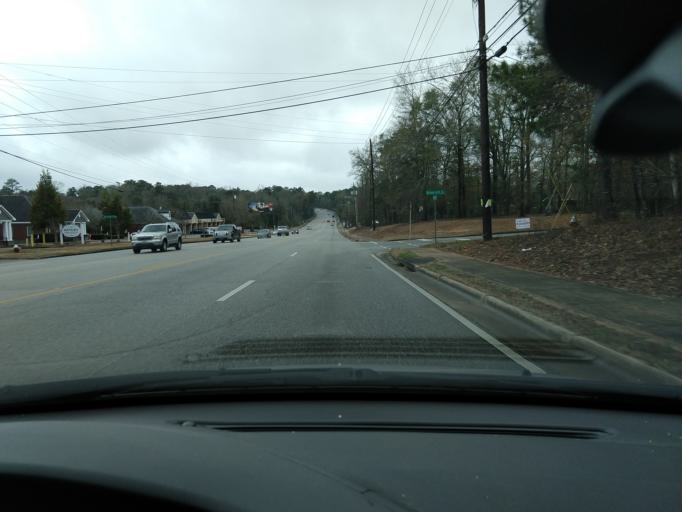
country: US
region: Alabama
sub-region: Houston County
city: Dothan
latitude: 31.2547
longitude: -85.4348
